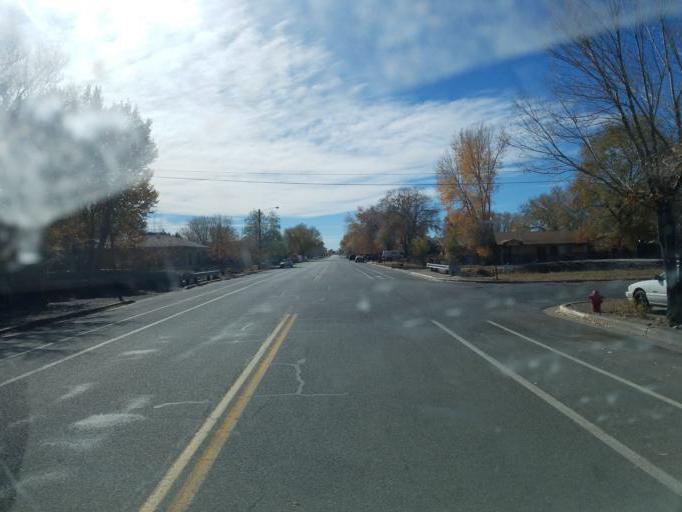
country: US
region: Colorado
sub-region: Alamosa County
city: Alamosa
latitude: 37.4565
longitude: -105.8701
